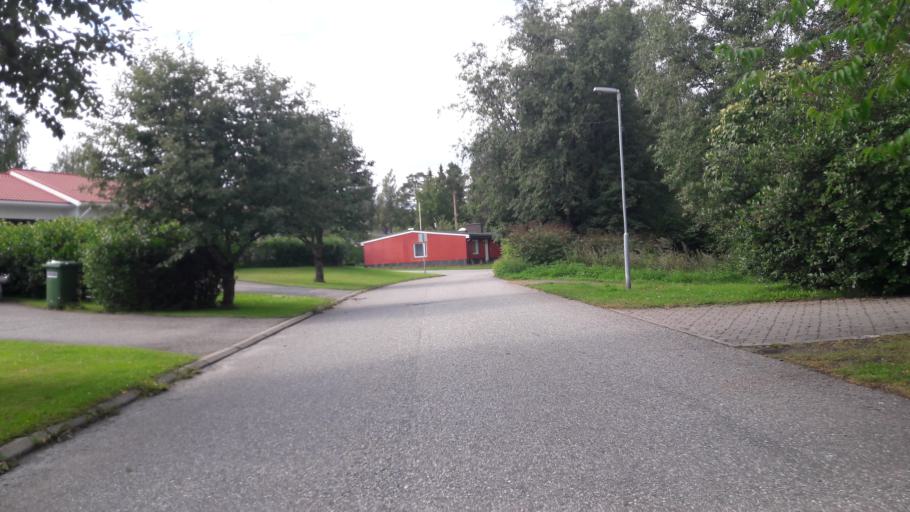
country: FI
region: North Karelia
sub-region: Joensuu
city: Joensuu
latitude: 62.5843
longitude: 29.8066
